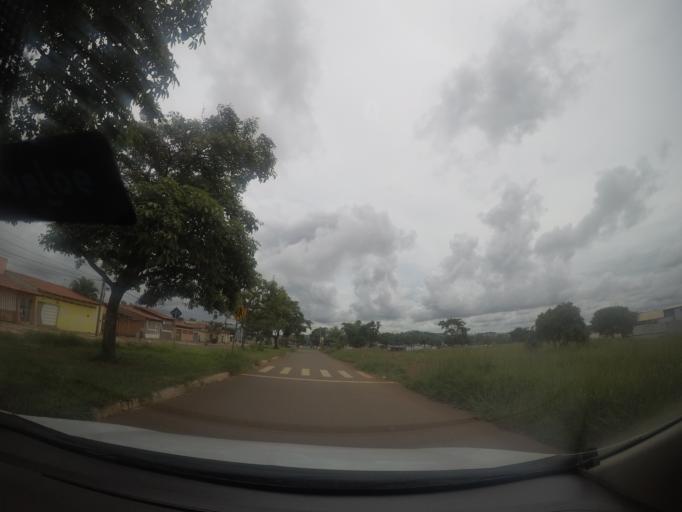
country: BR
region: Goias
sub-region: Trindade
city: Trindade
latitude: -16.6859
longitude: -49.3858
